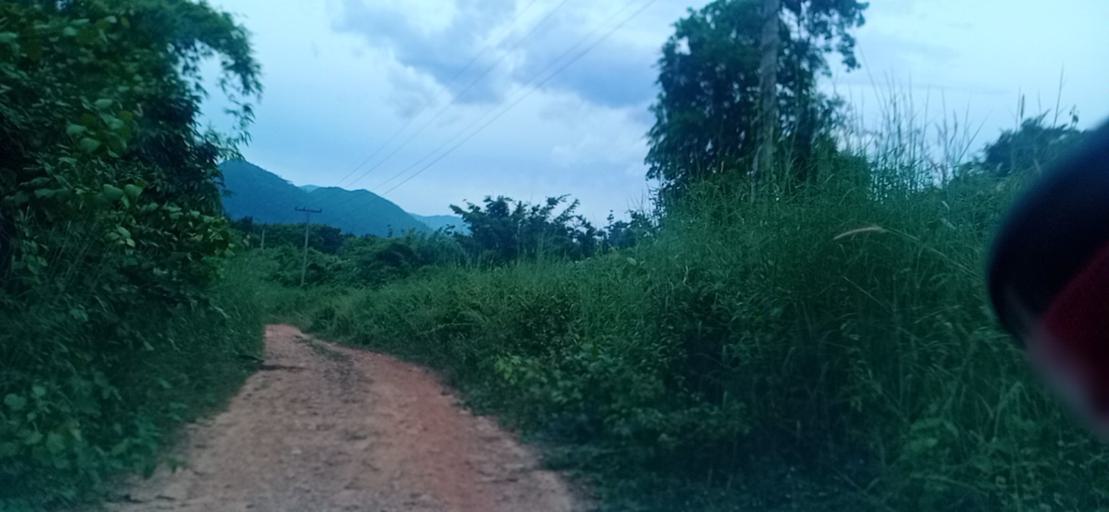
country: TH
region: Changwat Bueng Kan
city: Pak Khat
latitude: 18.5630
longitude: 103.2790
